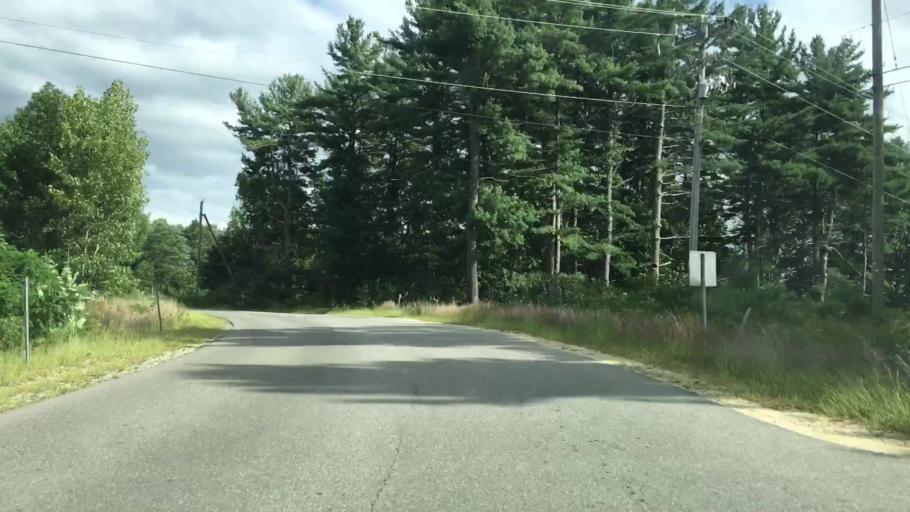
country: US
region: New Hampshire
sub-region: Strafford County
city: Madbury
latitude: 43.1696
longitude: -70.9194
